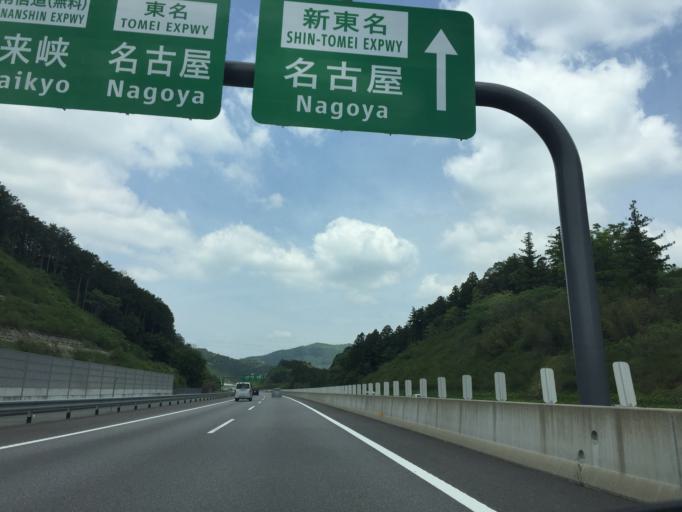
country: JP
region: Shizuoka
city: Hamakita
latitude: 34.8829
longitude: 137.6592
